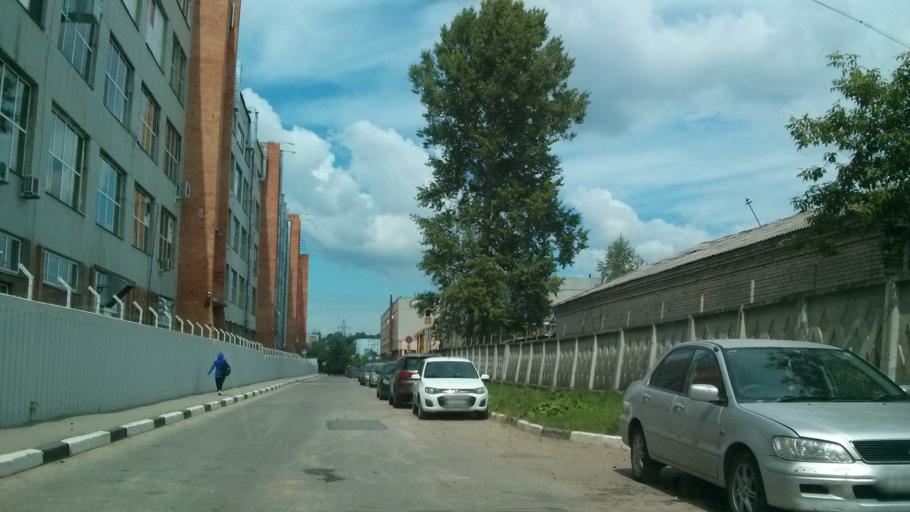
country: RU
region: Nizjnij Novgorod
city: Nizhniy Novgorod
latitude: 56.3013
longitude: 44.0178
